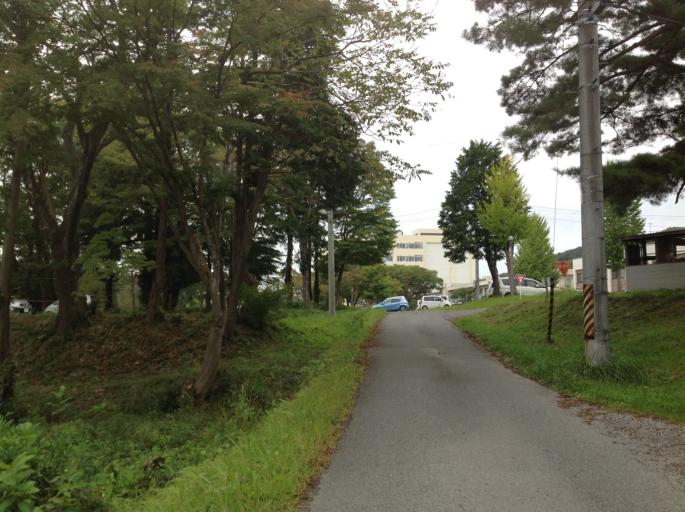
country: JP
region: Iwate
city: Ichinoseki
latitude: 38.9391
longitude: 141.1170
